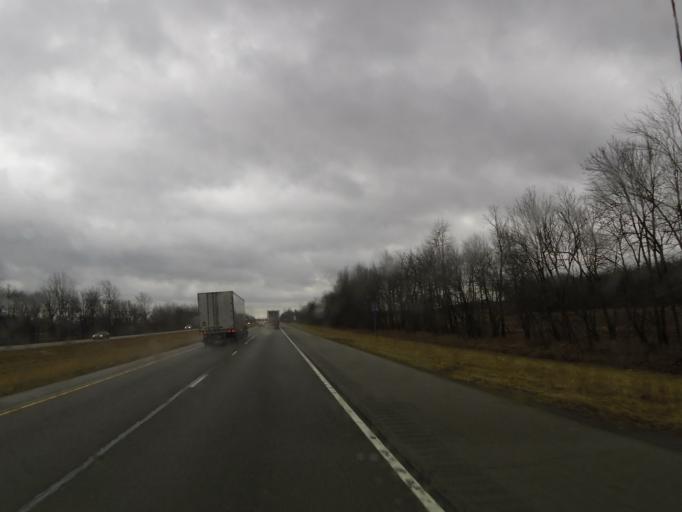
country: US
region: Illinois
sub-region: Massac County
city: Metropolis
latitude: 37.2931
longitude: -88.7508
